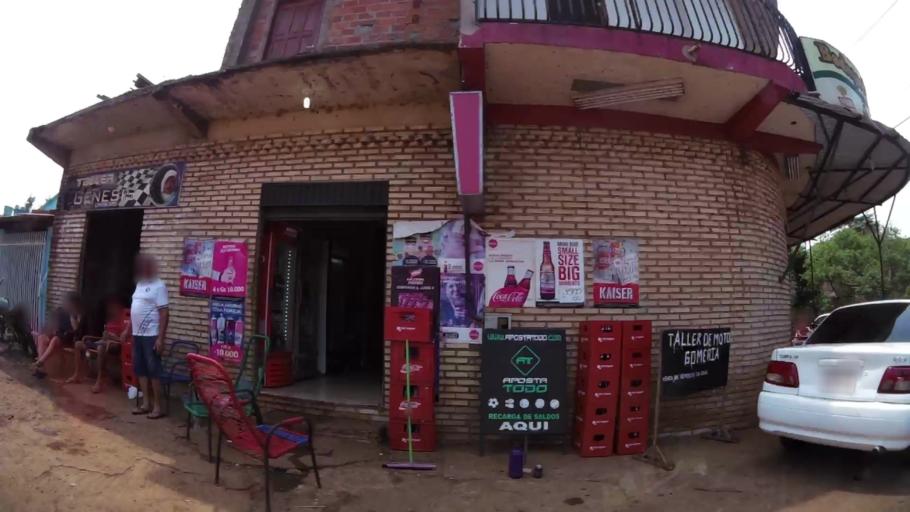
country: PY
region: Alto Parana
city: Ciudad del Este
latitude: -25.4993
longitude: -54.6289
